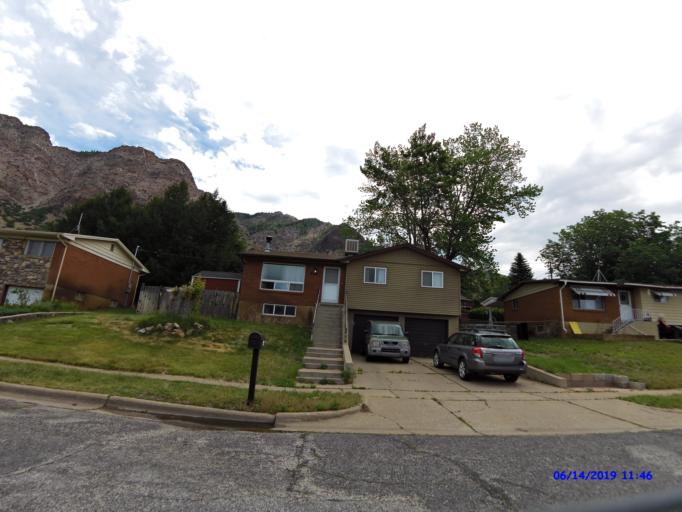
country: US
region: Utah
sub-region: Weber County
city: Ogden
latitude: 41.2551
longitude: -111.9414
